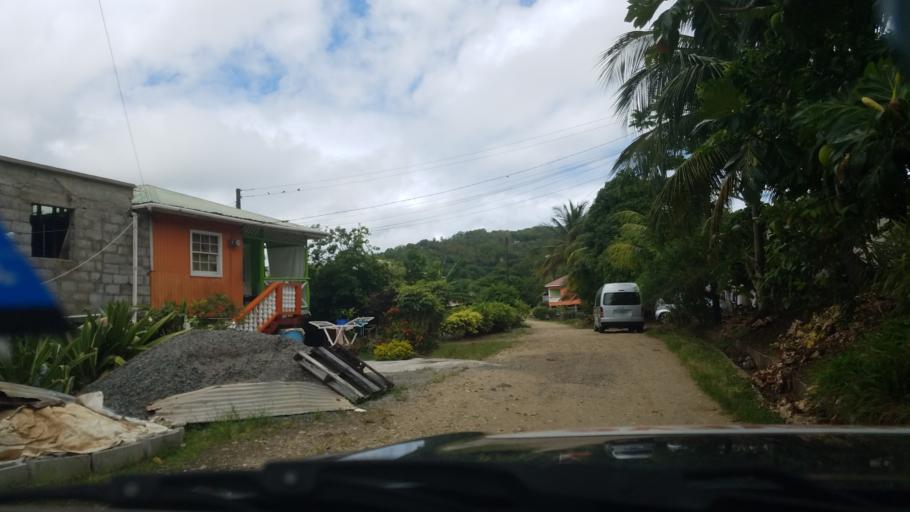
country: LC
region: Castries Quarter
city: Bisee
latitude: 14.0114
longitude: -60.9190
